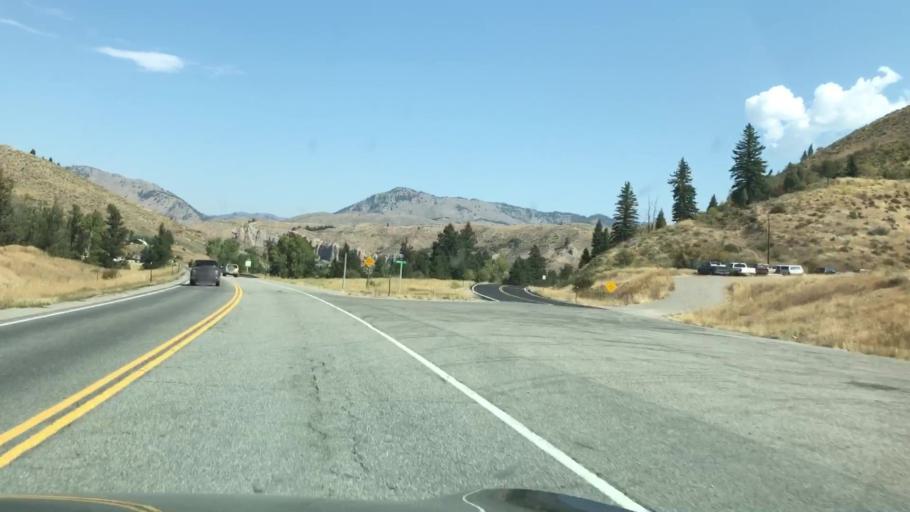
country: US
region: Wyoming
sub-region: Teton County
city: Hoback
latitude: 43.3420
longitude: -110.7224
